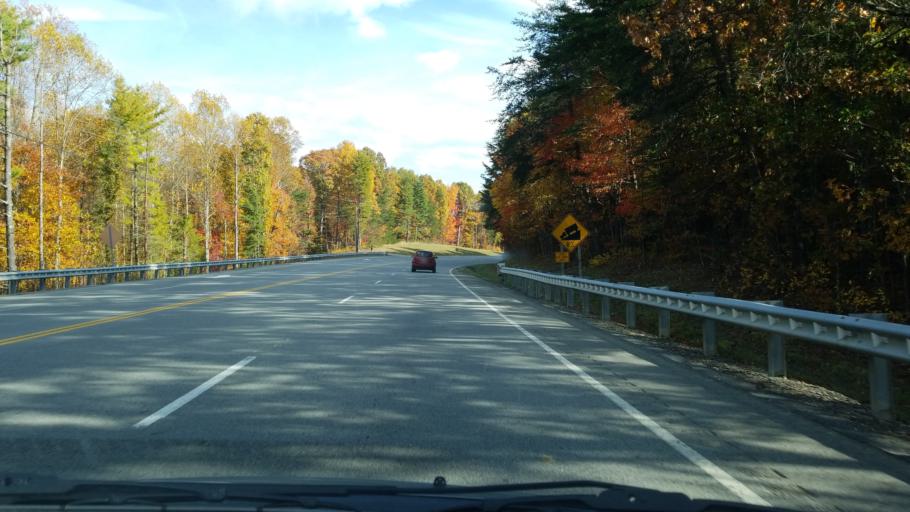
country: US
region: Tennessee
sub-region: Sequatchie County
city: Dunlap
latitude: 35.4390
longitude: -85.4230
